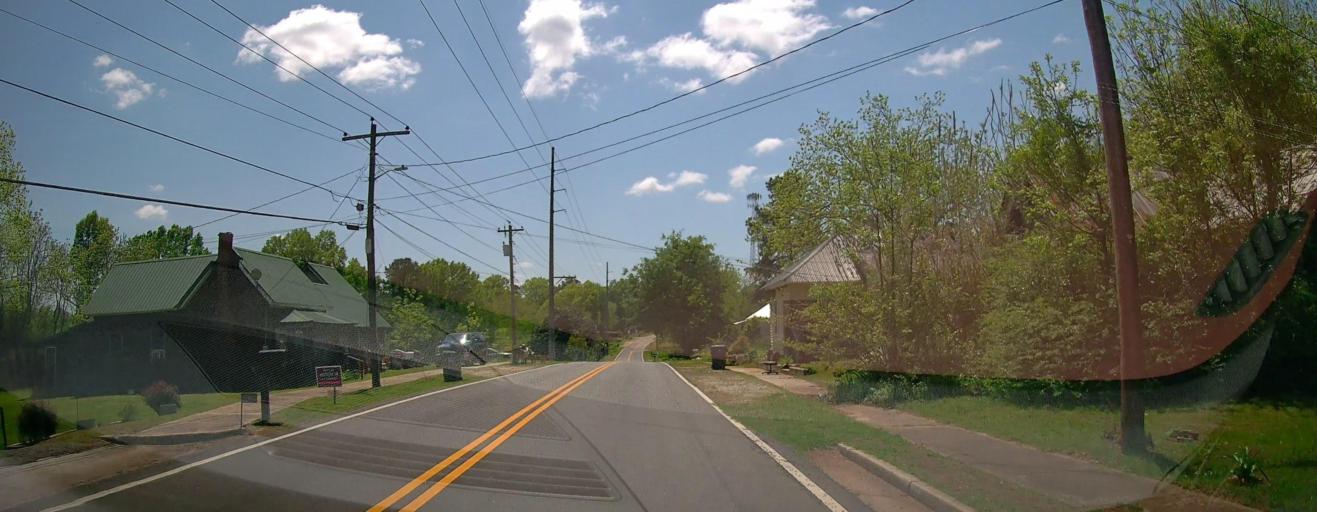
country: US
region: Georgia
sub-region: Jasper County
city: Monticello
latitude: 33.2966
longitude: -83.6887
